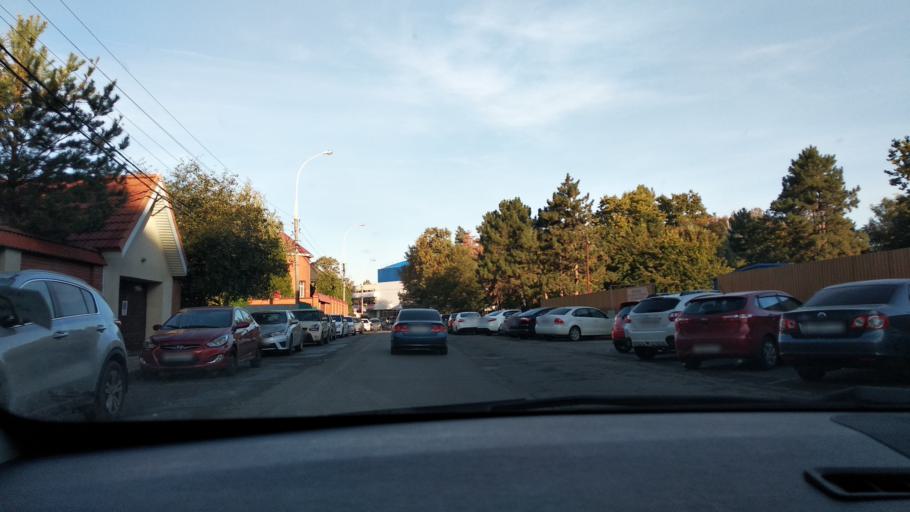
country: RU
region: Adygeya
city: Yablonovskiy
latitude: 45.0150
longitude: 38.9572
